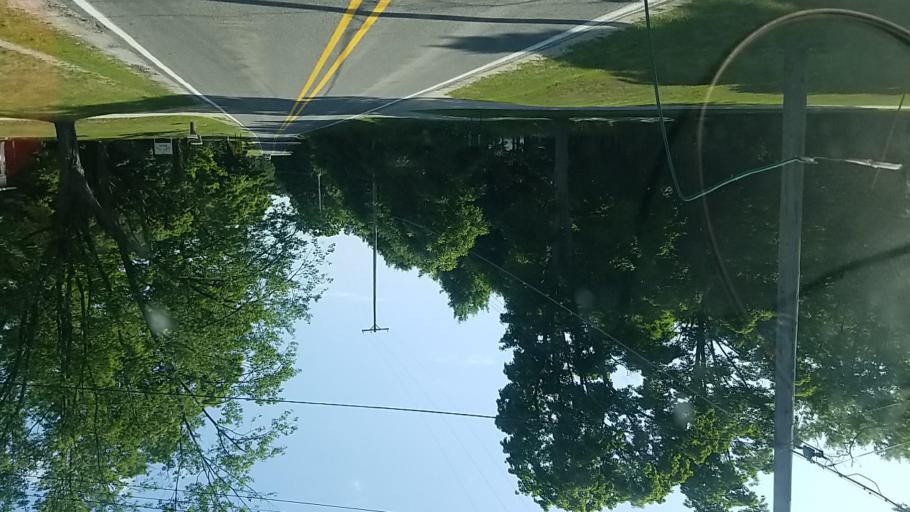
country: US
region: Michigan
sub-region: Muskegon County
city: Whitehall
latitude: 43.3733
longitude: -86.3764
